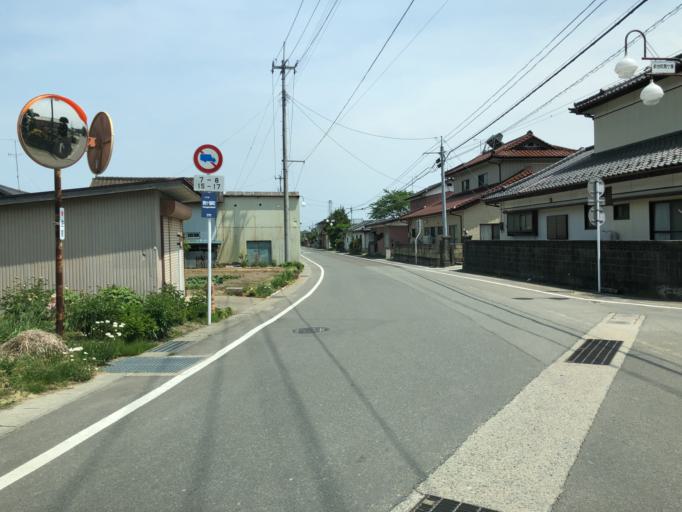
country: JP
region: Miyagi
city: Marumori
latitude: 37.8484
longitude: 140.9148
